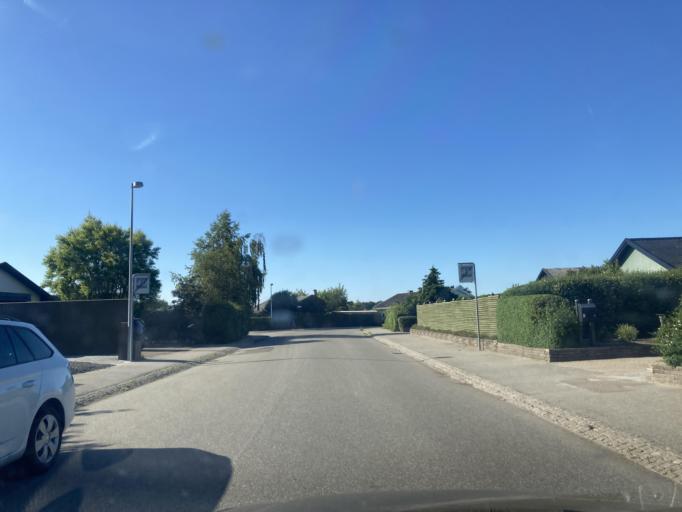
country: DK
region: Capital Region
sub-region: Halsnaes Kommune
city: Frederiksvaerk
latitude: 55.9858
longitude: 12.0050
